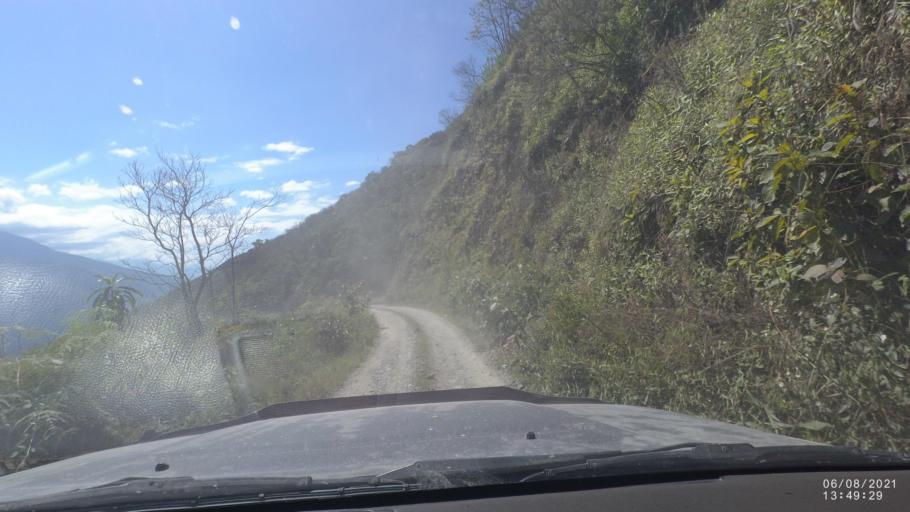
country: BO
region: La Paz
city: Quime
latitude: -16.6609
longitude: -66.7218
